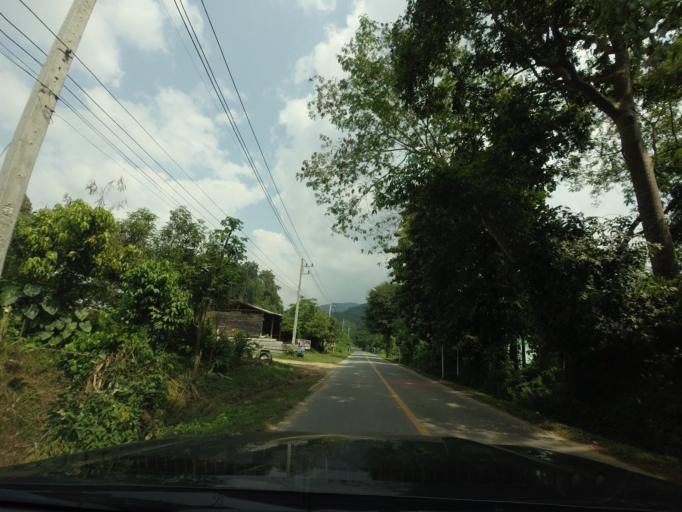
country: TH
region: Nan
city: Pua
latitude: 19.1759
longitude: 100.9525
